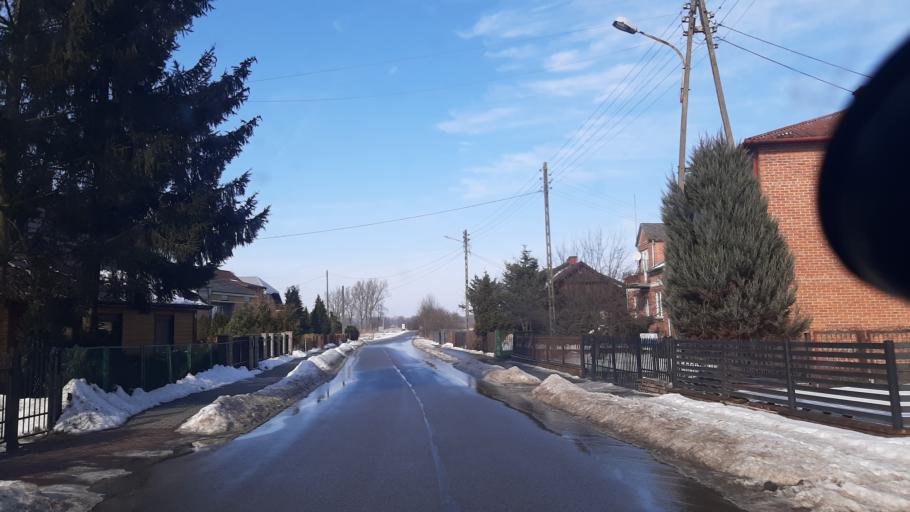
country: PL
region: Lublin Voivodeship
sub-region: Powiat pulawski
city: Baranow
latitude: 51.5598
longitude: 22.1354
